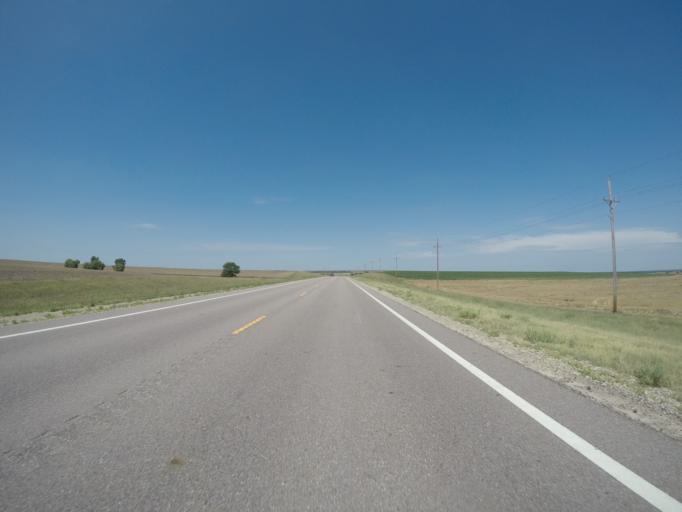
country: US
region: Kansas
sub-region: Osborne County
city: Osborne
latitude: 39.5101
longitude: -98.6845
